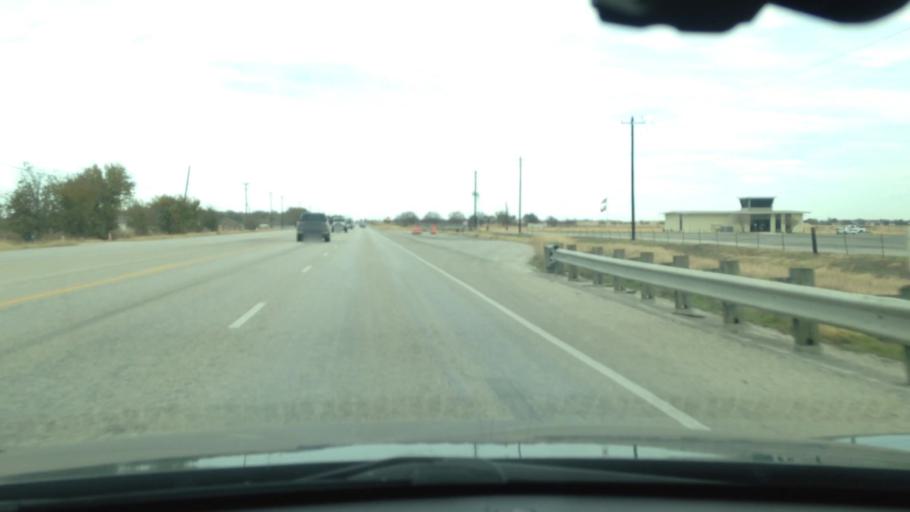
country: US
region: Texas
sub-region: Caldwell County
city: Martindale
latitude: 29.9019
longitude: -97.8691
